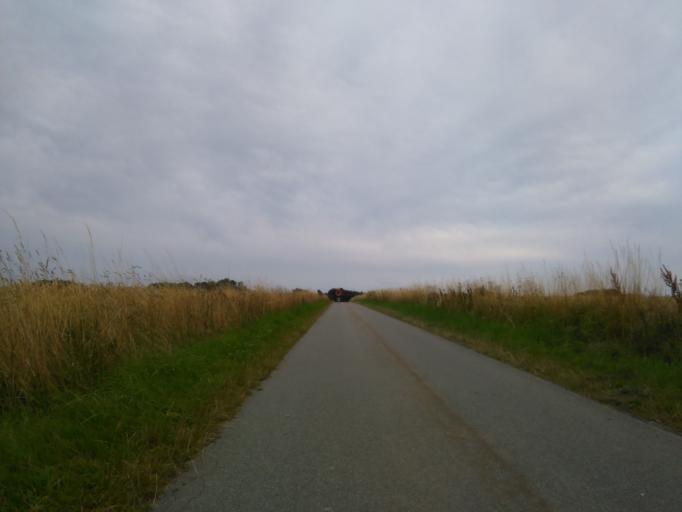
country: DK
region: Central Jutland
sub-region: Odder Kommune
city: Odder
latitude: 55.8612
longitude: 10.0624
